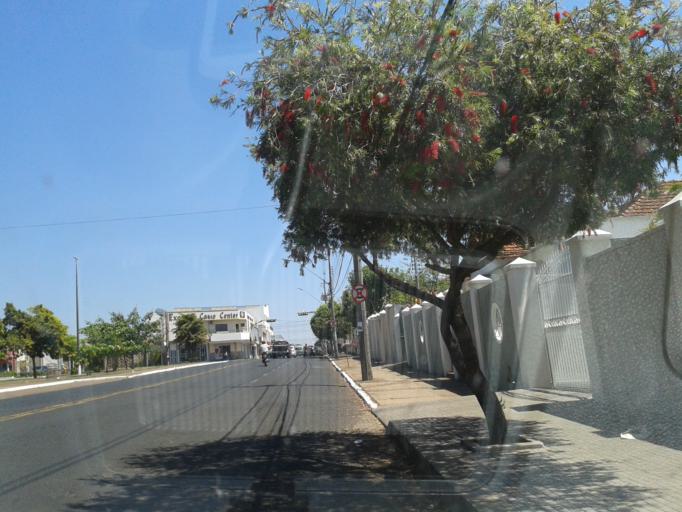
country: BR
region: Minas Gerais
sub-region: Araguari
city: Araguari
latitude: -18.6457
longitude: -48.1991
